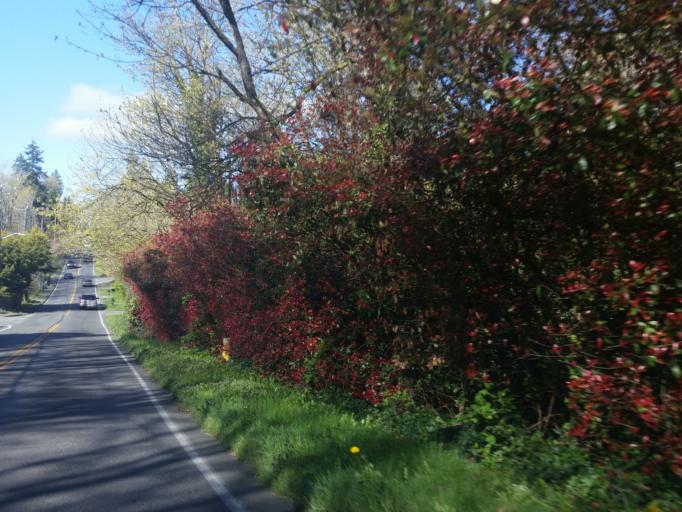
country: US
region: Washington
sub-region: King County
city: Shoreline
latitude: 47.7108
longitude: -122.3608
